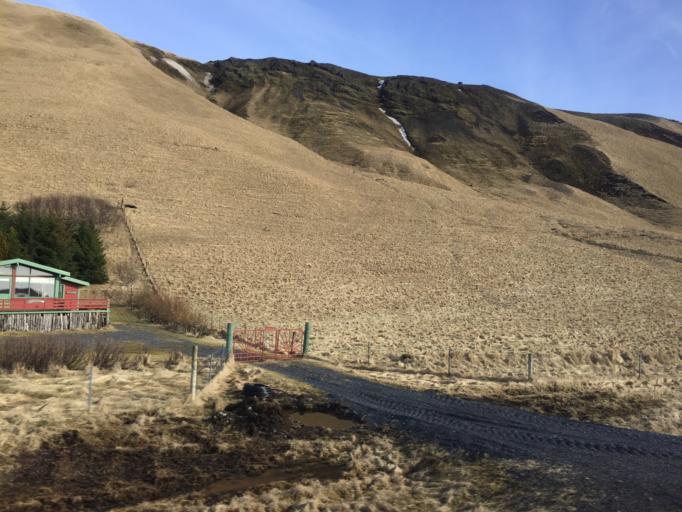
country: IS
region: South
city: Vestmannaeyjar
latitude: 63.4117
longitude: -19.0481
